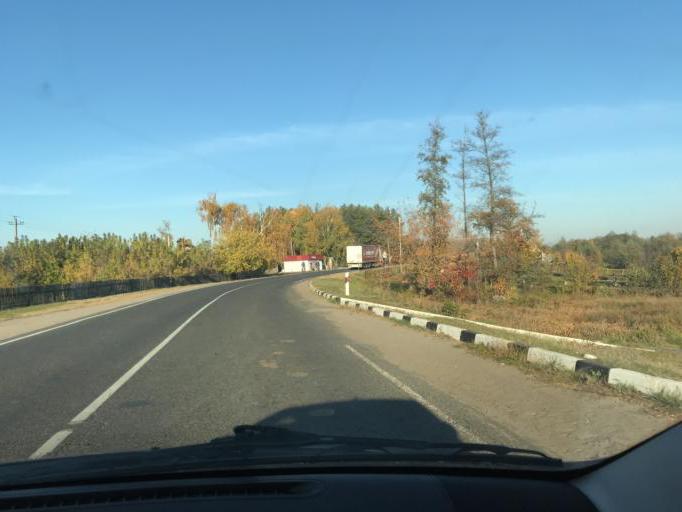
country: BY
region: Brest
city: Stolin
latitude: 51.8306
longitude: 26.7153
